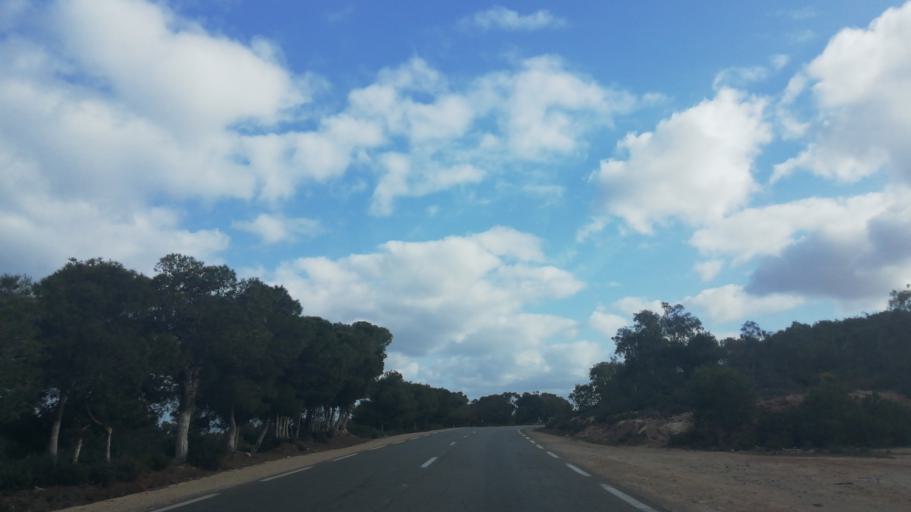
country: DZ
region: Relizane
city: Mazouna
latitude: 36.2369
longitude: 0.5247
